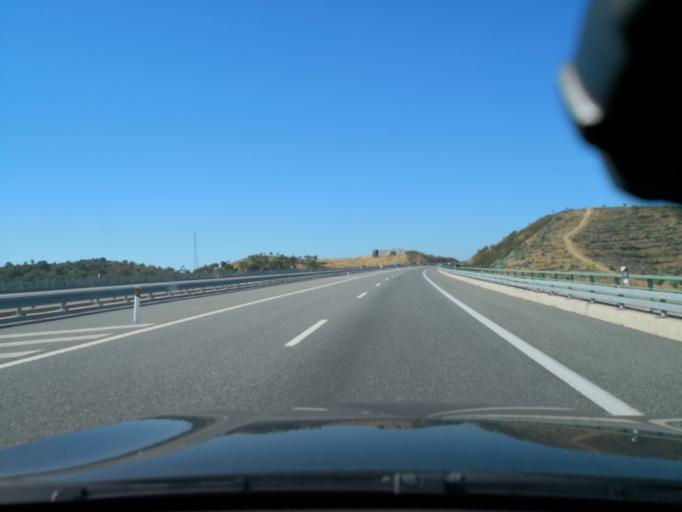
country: PT
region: Faro
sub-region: Silves
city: Sao Bartolomeu de Messines
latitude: 37.3058
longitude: -8.2548
